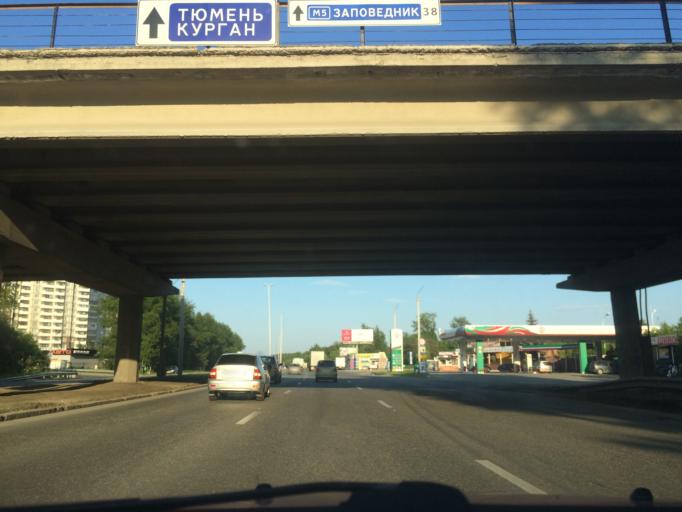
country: RU
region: Sverdlovsk
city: Yekaterinburg
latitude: 56.8247
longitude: 60.6918
